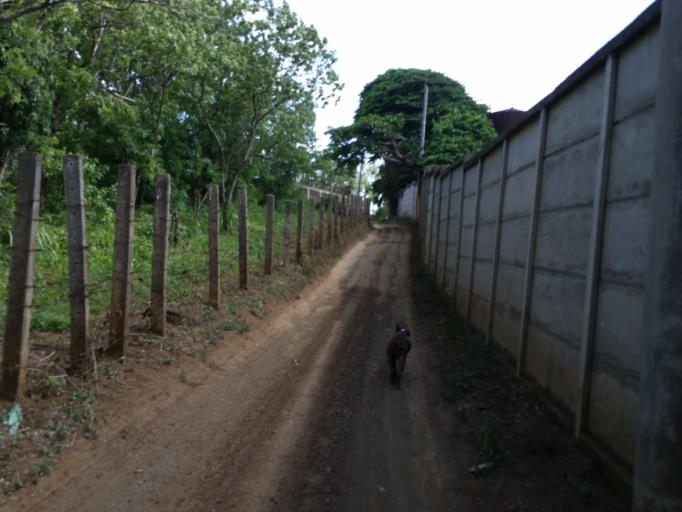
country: NI
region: Managua
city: Managua
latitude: 12.0809
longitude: -86.2505
